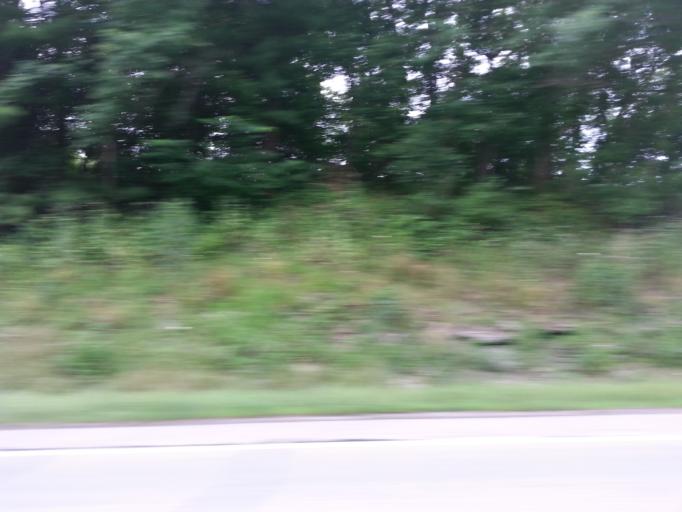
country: US
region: Ohio
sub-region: Brown County
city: Georgetown
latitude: 38.8379
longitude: -83.8422
